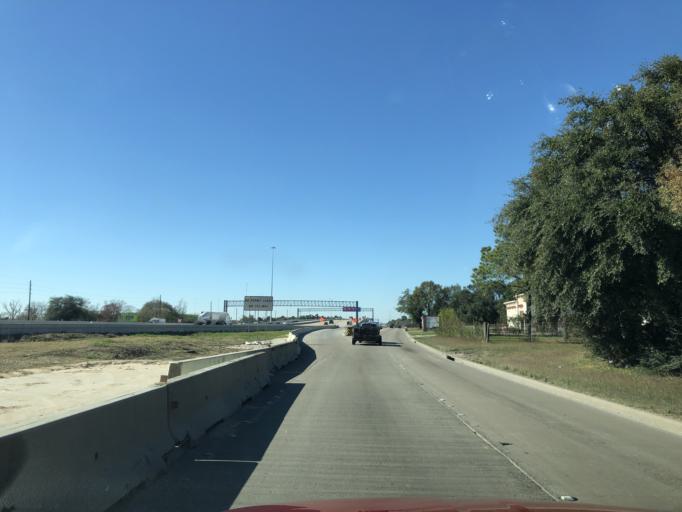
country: US
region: Texas
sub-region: Brazoria County
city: Brookside Village
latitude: 29.5976
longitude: -95.3941
